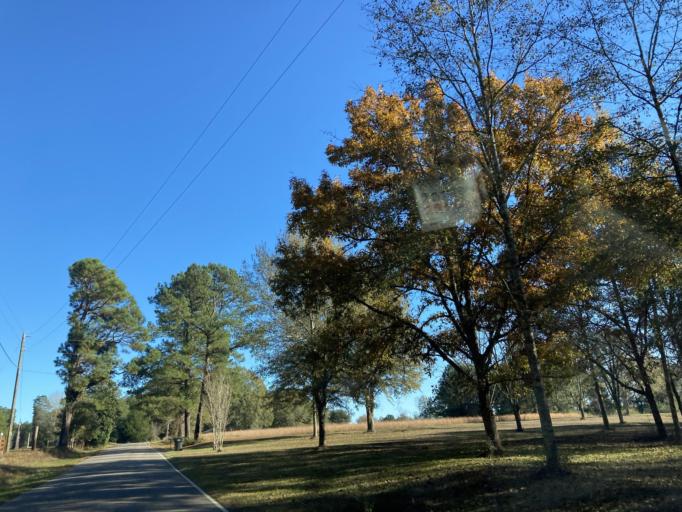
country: US
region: Mississippi
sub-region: Lamar County
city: Sumrall
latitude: 31.3665
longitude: -89.5742
